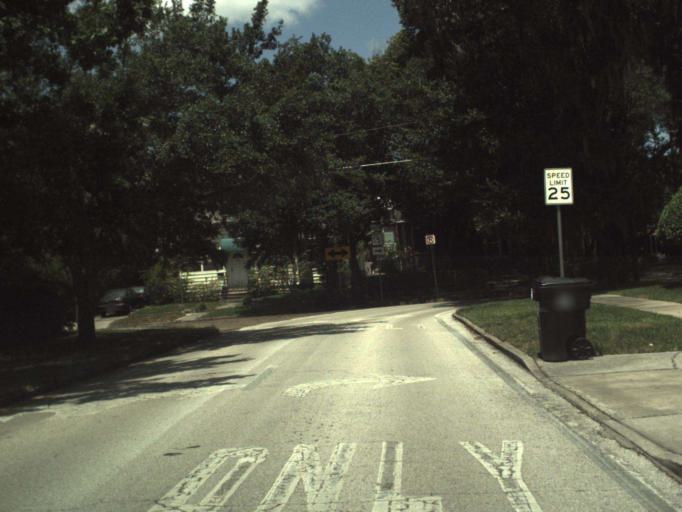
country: US
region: Florida
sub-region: Orange County
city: Orlando
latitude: 28.5446
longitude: -81.3637
